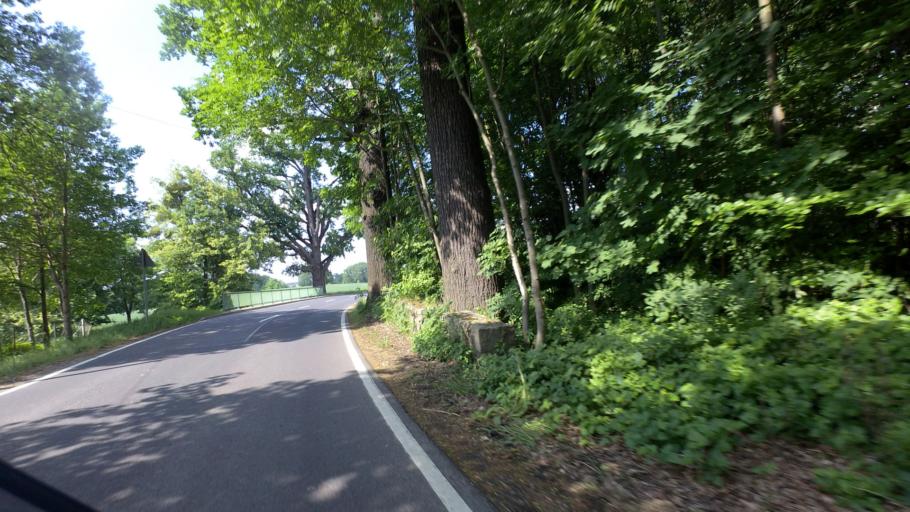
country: DE
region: Saxony
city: Hochkirch
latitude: 51.1960
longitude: 14.5992
